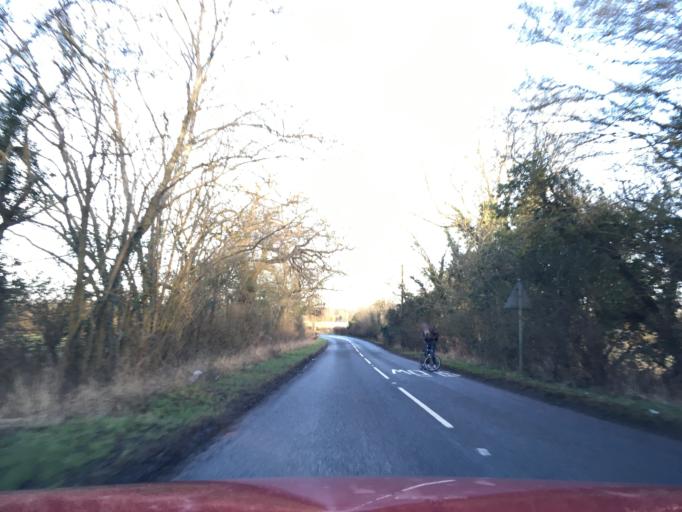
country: GB
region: England
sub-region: Warwickshire
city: Henley in Arden
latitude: 52.2544
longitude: -1.7906
